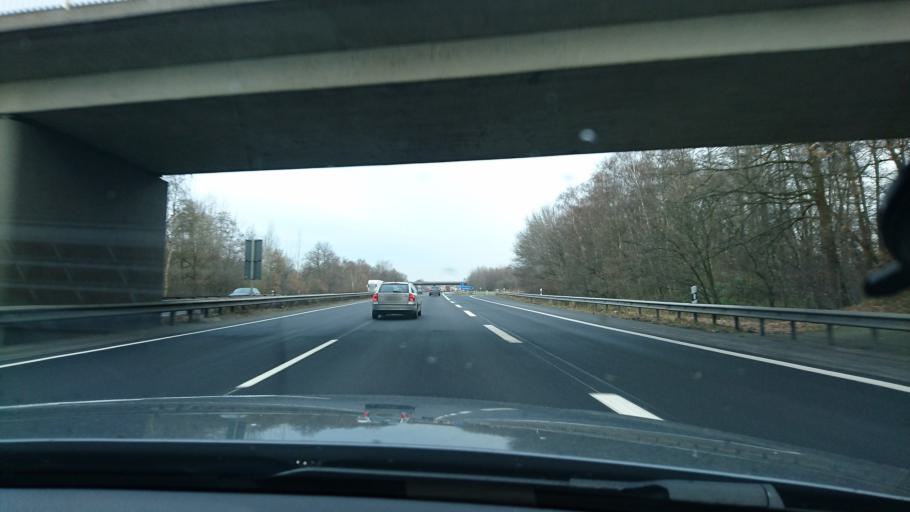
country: DE
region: Lower Saxony
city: Holdorf
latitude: 52.5933
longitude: 8.1122
